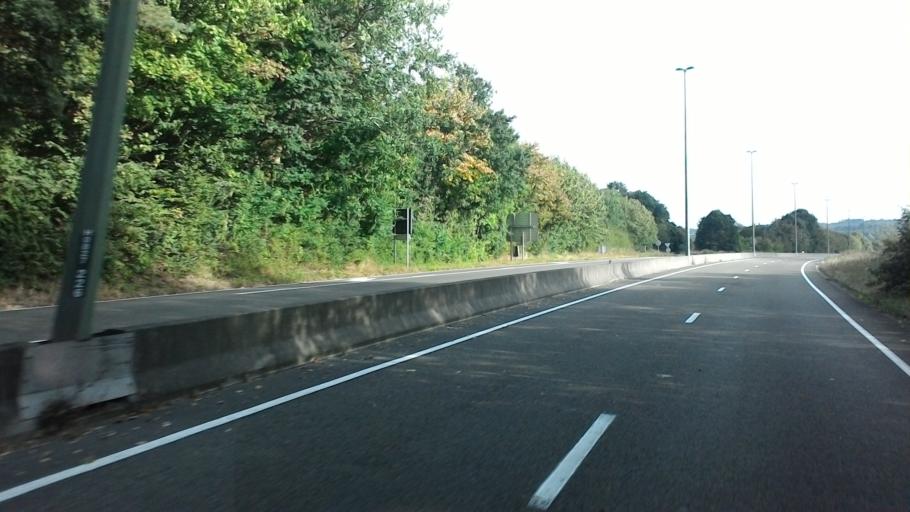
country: BE
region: Wallonia
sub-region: Province du Luxembourg
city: Attert
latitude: 49.7601
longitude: 5.7742
